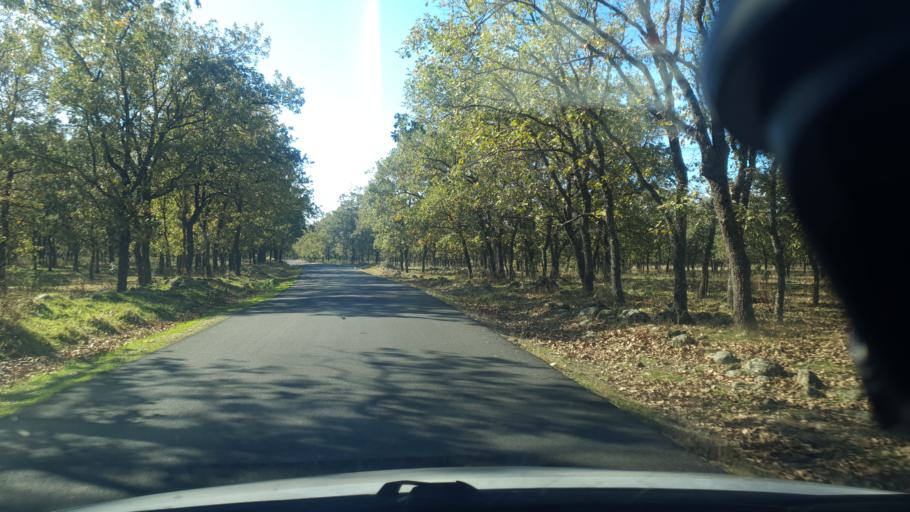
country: ES
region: Castille and Leon
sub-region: Provincia de Avila
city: Candeleda
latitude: 40.1328
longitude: -5.2644
